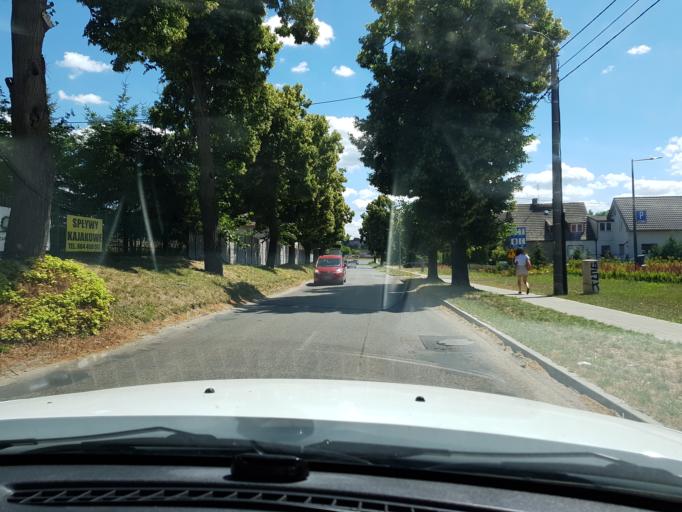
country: PL
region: West Pomeranian Voivodeship
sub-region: Powiat mysliborski
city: Mysliborz
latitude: 52.9229
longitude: 14.8801
